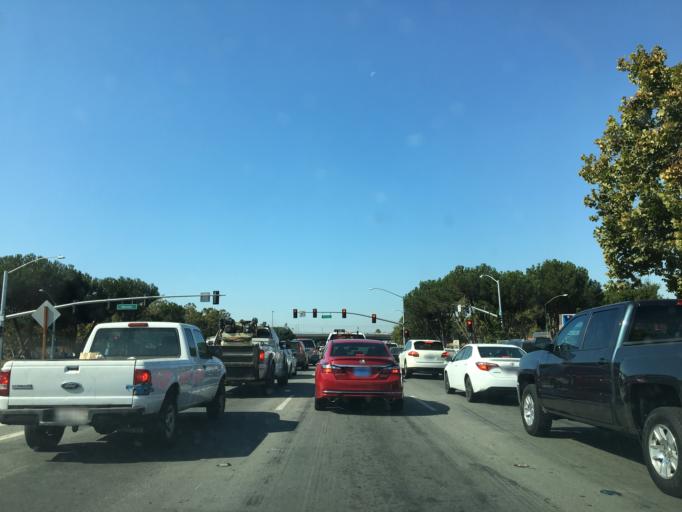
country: US
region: California
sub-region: Santa Clara County
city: Seven Trees
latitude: 37.2745
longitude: -121.8594
